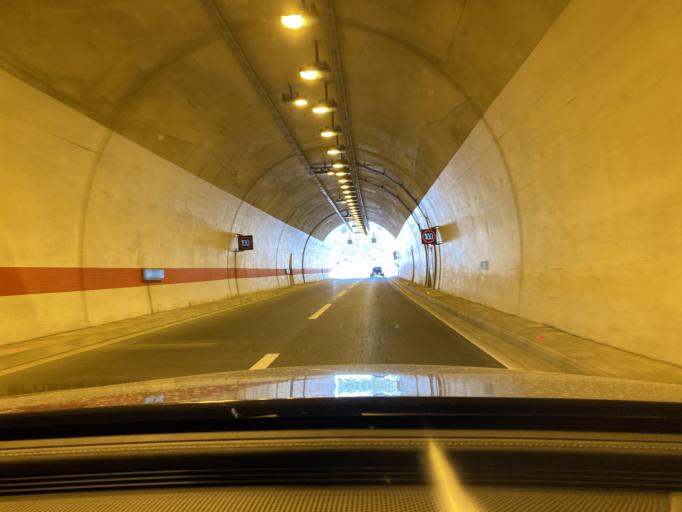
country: HR
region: Dubrovacko-Neretvanska
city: Komin
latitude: 43.1153
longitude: 17.4808
